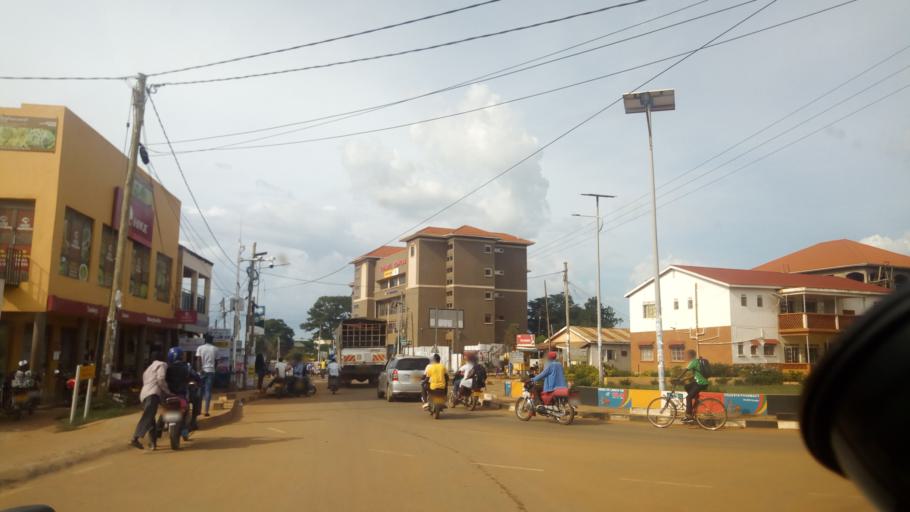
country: UG
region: Northern Region
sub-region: Lira District
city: Lira
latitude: 2.2379
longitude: 32.8935
